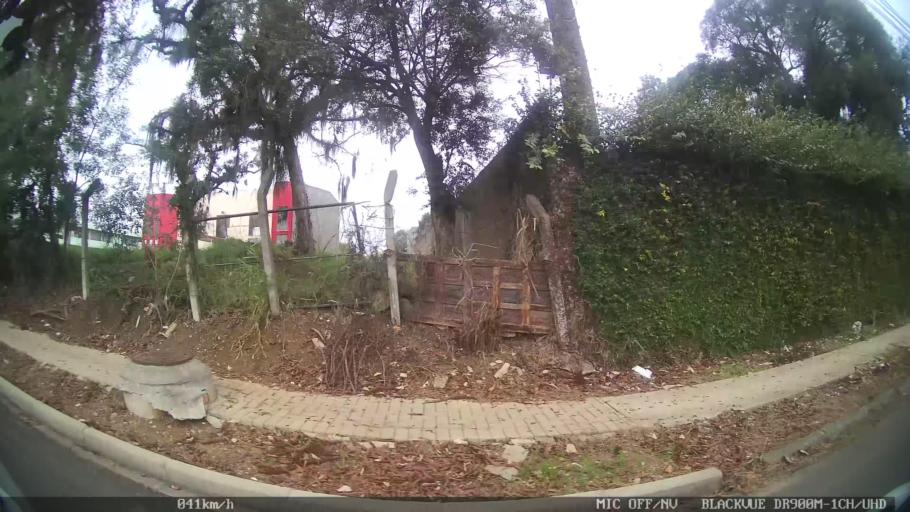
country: BR
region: Parana
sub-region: Curitiba
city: Curitiba
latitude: -25.3962
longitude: -49.3182
